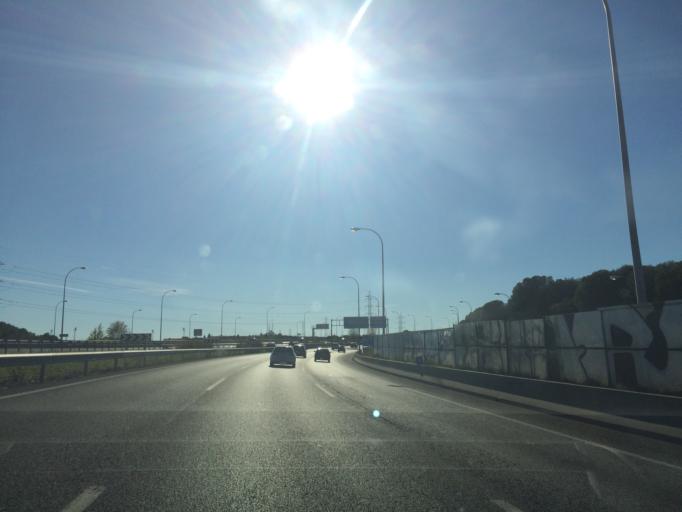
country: ES
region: Madrid
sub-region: Provincia de Madrid
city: Pozuelo de Alarcon
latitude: 40.4106
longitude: -3.8222
